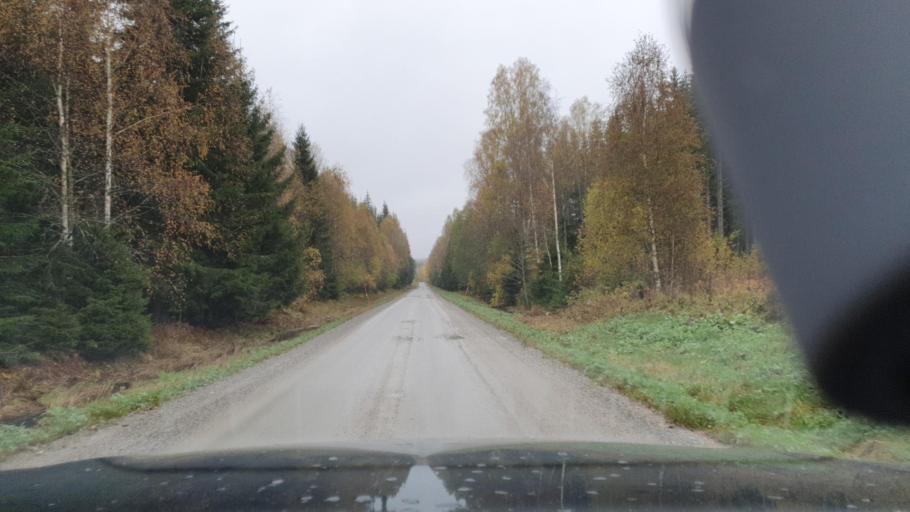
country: SE
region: Vaermland
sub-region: Arvika Kommun
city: Arvika
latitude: 59.8044
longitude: 12.7485
